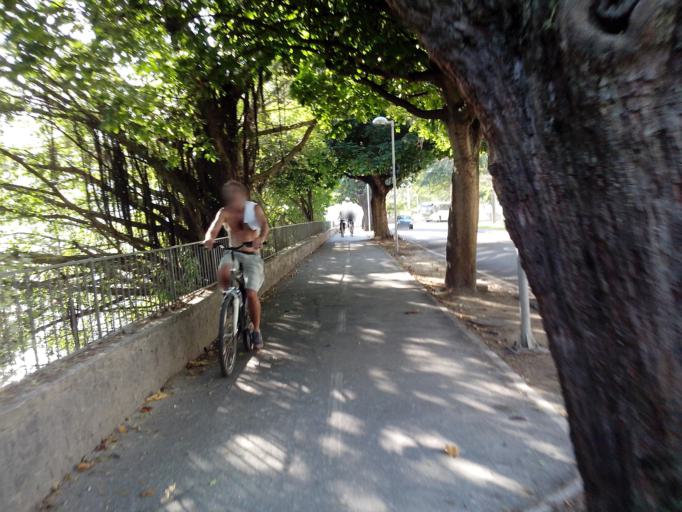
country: BR
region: Rio de Janeiro
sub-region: Rio De Janeiro
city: Rio de Janeiro
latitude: -22.9733
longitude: -43.2081
